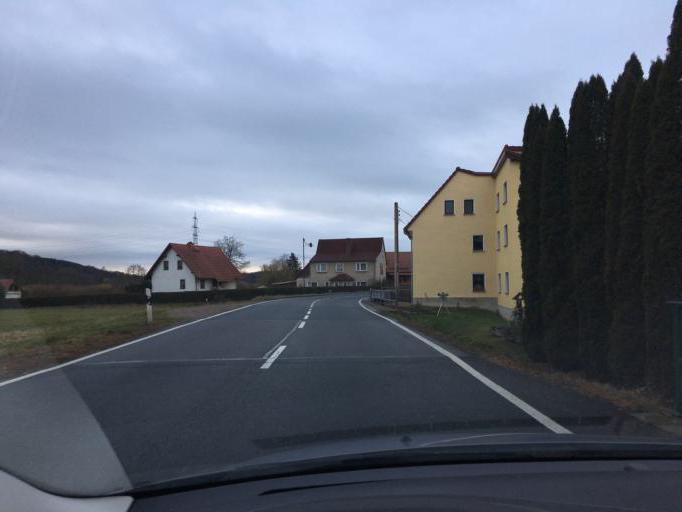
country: DE
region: Thuringia
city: Juckelberg
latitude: 50.8956
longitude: 12.6325
